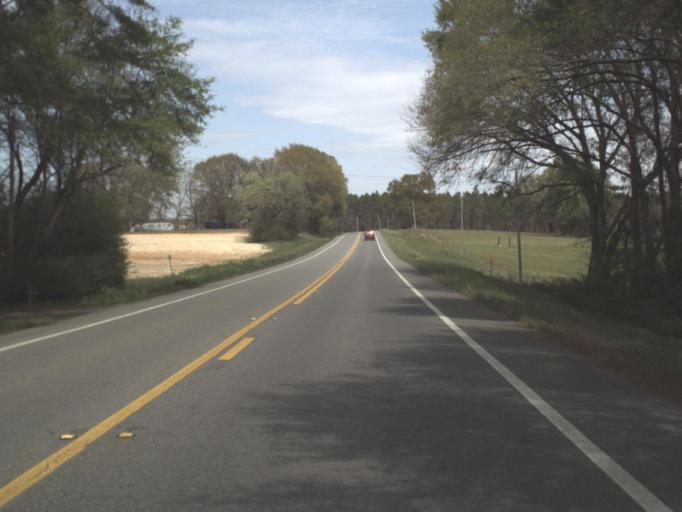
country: US
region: Florida
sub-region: Washington County
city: Chipley
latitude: 30.8402
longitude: -85.5012
